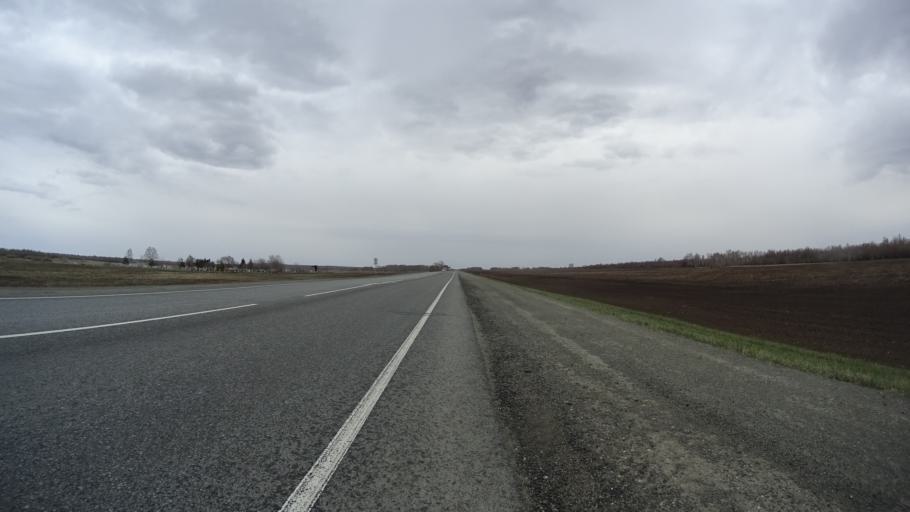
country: RU
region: Chelyabinsk
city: Krasnogorskiy
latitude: 54.6701
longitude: 61.2509
